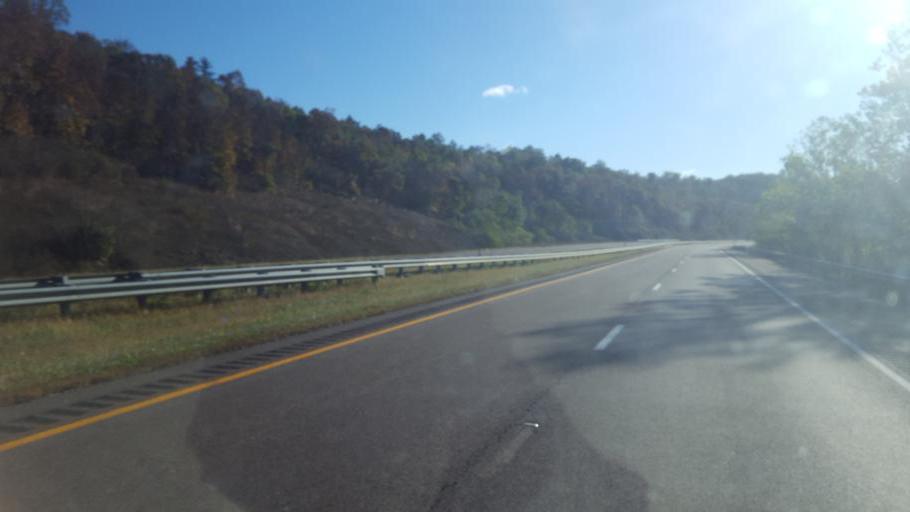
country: US
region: West Virginia
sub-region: Morgan County
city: Berkeley Springs
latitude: 39.6813
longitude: -78.4868
